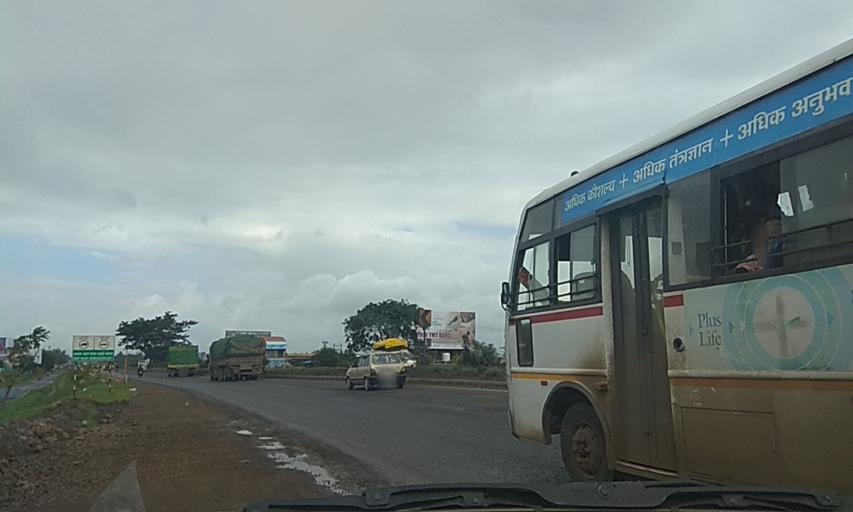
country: IN
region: Maharashtra
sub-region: Kolhapur
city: Kolhapur
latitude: 16.7208
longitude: 74.2829
